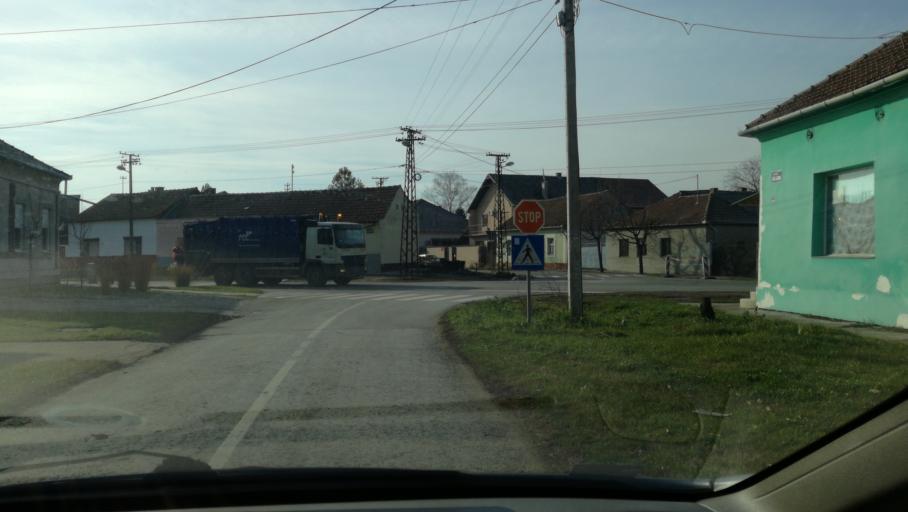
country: RS
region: Autonomna Pokrajina Vojvodina
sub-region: Severnobanatski Okrug
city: Kikinda
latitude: 45.8379
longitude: 20.4697
